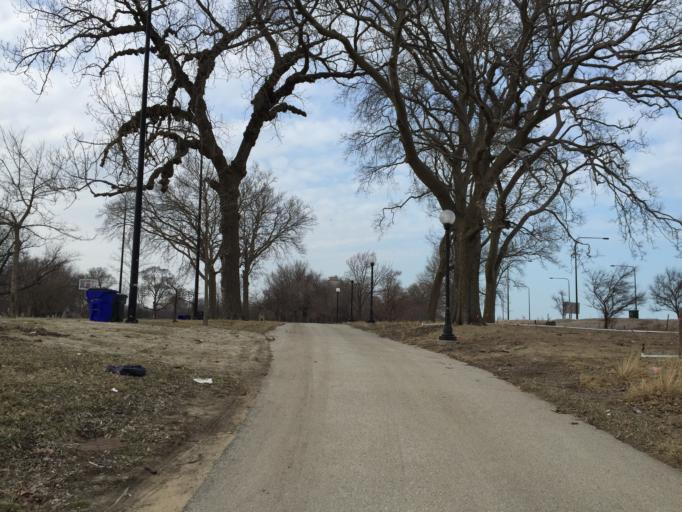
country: US
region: Illinois
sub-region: Cook County
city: Chicago
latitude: 41.7817
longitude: -87.5759
